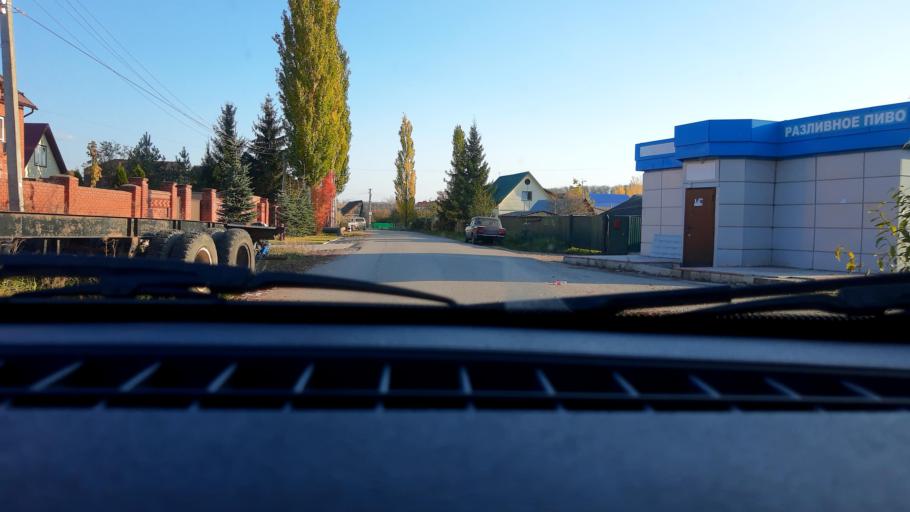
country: RU
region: Bashkortostan
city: Mikhaylovka
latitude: 54.7855
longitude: 55.8989
